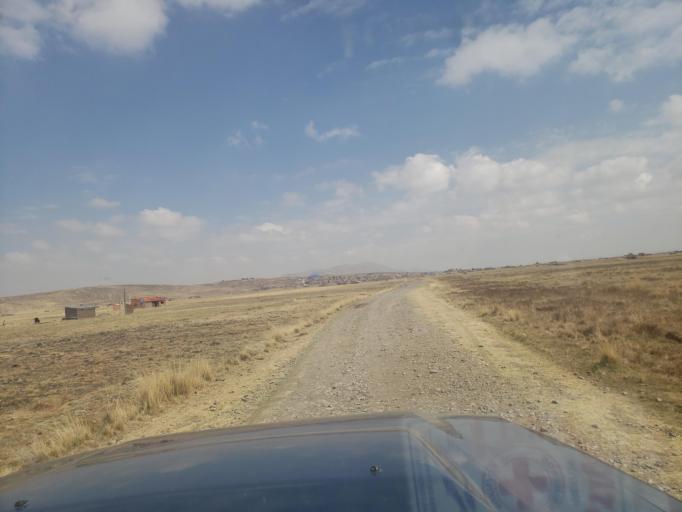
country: BO
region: La Paz
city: Batallas
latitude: -16.4054
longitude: -68.4569
